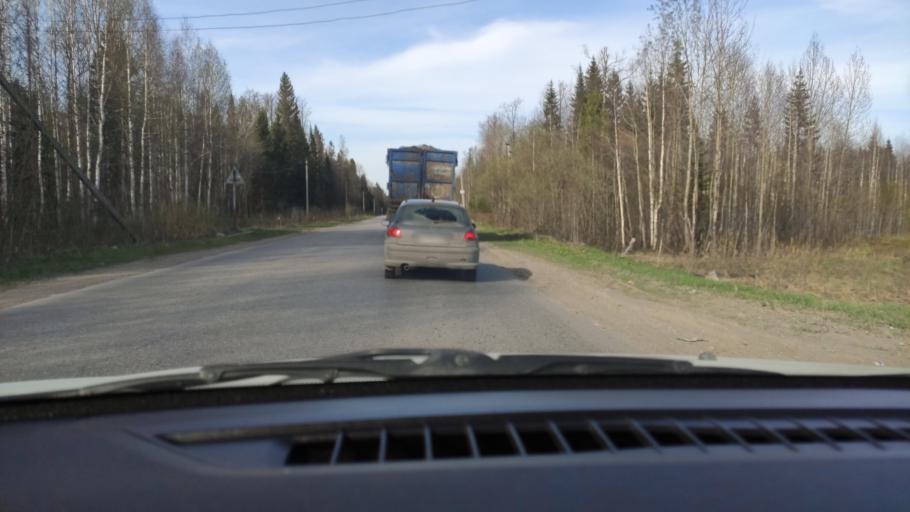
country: RU
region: Perm
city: Novyye Lyady
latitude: 57.9407
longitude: 56.4952
